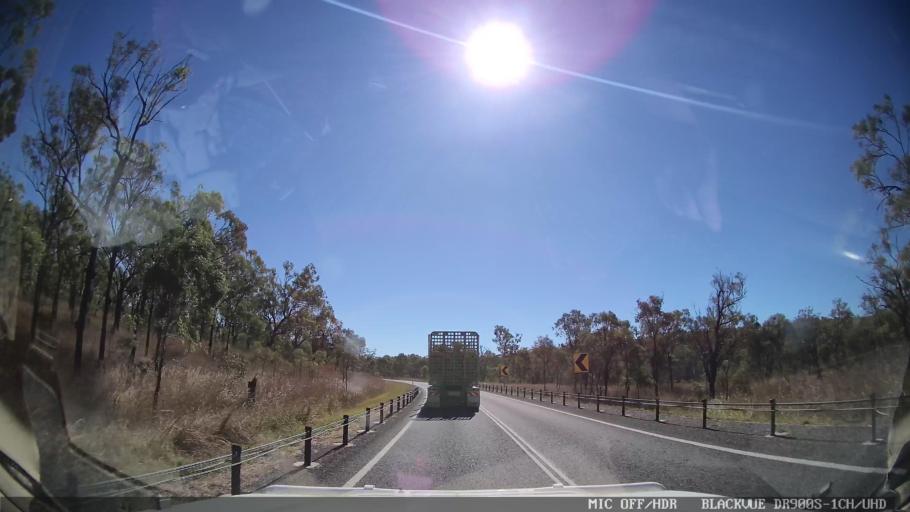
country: AU
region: Queensland
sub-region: Gladstone
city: Toolooa
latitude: -24.1517
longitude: 151.2101
